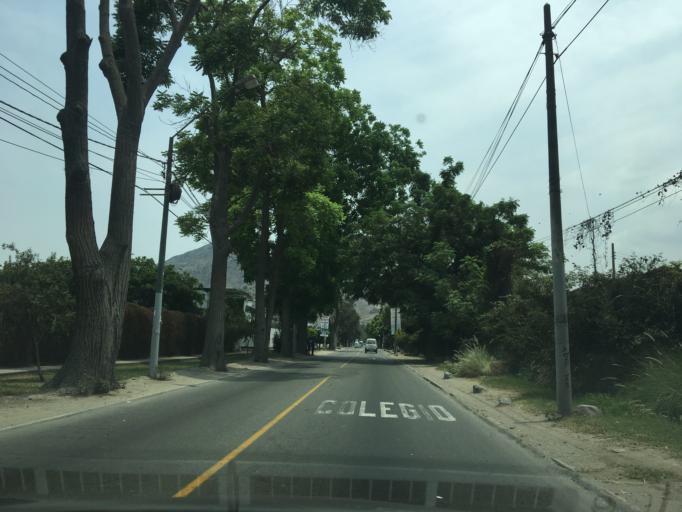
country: PE
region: Lima
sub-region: Lima
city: La Molina
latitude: -12.0774
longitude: -76.9439
